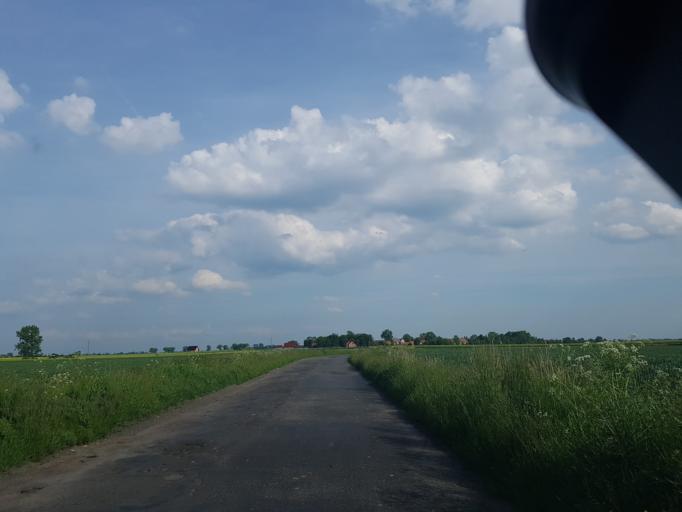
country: PL
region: Lower Silesian Voivodeship
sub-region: Powiat olawski
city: Wierzbno
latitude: 50.8745
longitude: 17.1500
